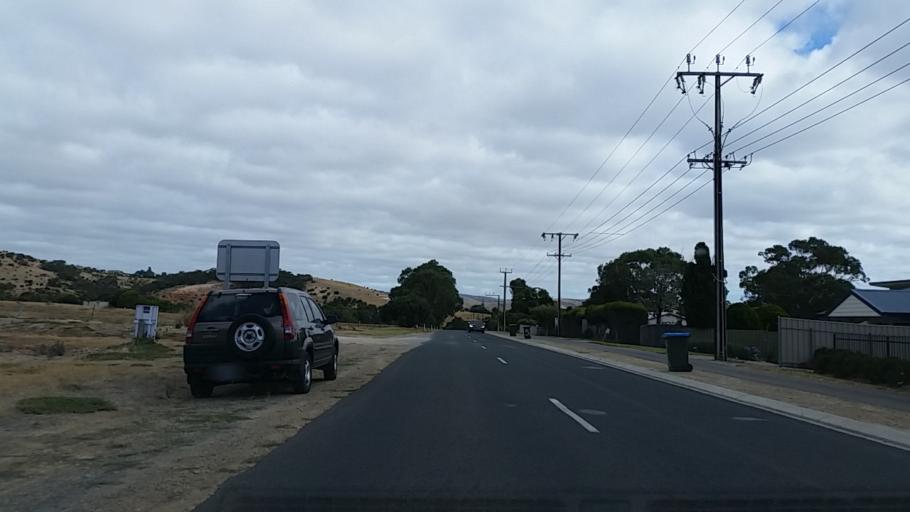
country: AU
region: South Australia
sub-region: Yankalilla
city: Normanville
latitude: -35.4280
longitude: 138.3268
